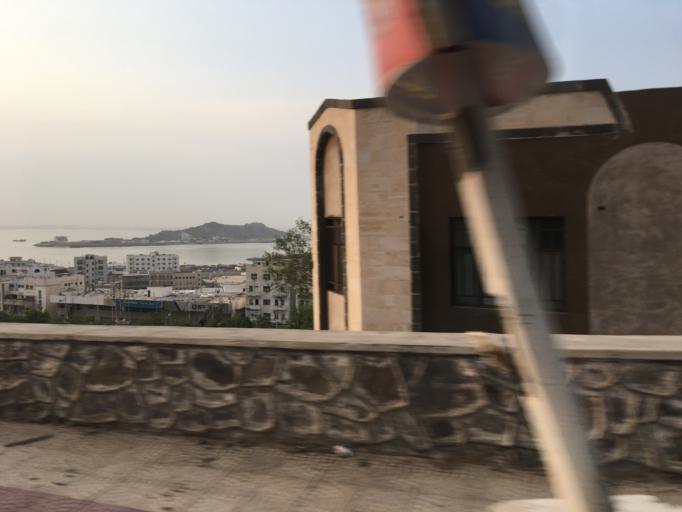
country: YE
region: Aden
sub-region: Craiter
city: Crater
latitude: 12.7886
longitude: 45.0230
